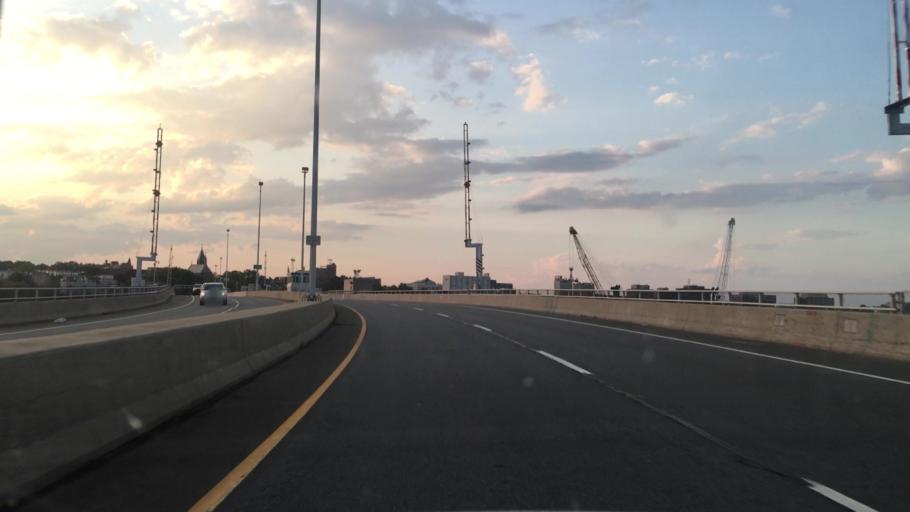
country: US
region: Maine
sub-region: Cumberland County
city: South Portland
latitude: 43.6437
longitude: -70.2568
